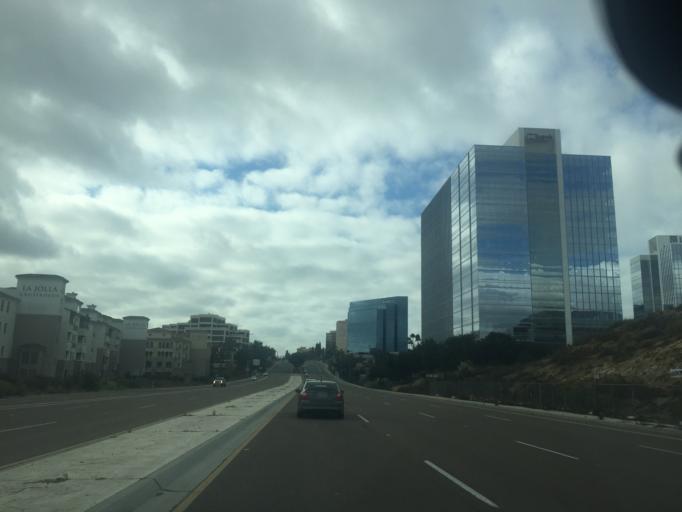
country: US
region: California
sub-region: San Diego County
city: La Jolla
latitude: 32.8748
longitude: -117.2022
